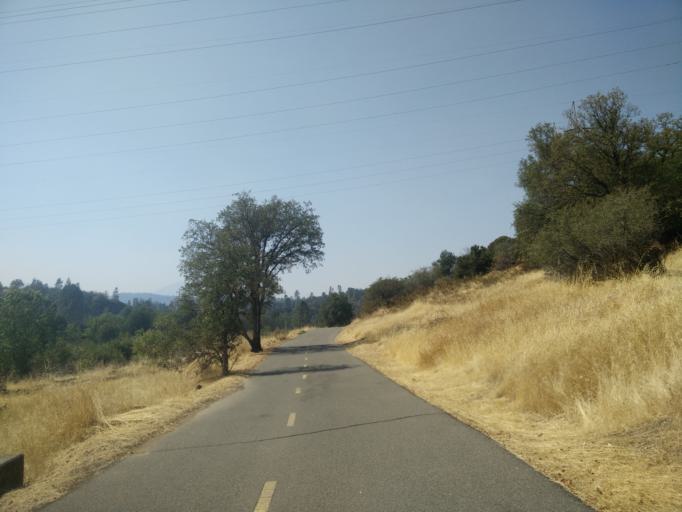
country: US
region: California
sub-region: Shasta County
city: Redding
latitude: 40.5950
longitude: -122.4339
